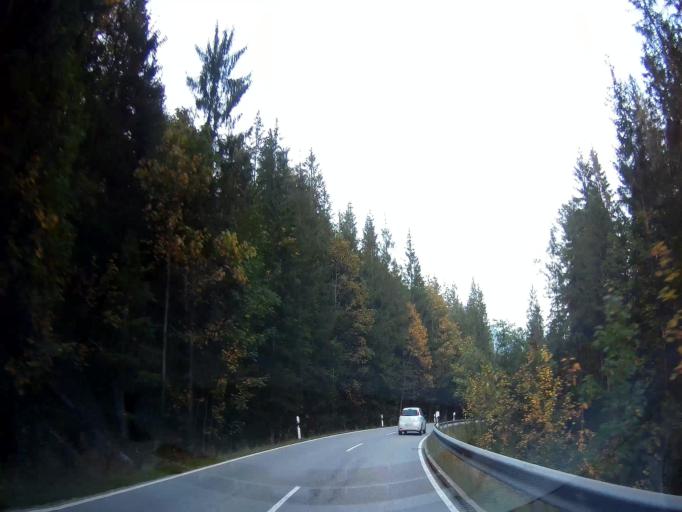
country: DE
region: Bavaria
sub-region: Upper Bavaria
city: Bischofswiesen
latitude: 47.6435
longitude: 12.9184
